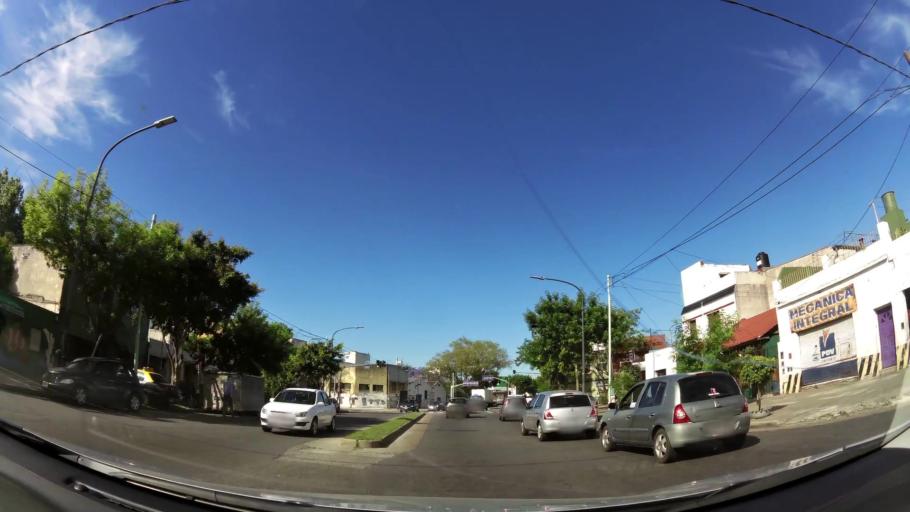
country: AR
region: Buenos Aires
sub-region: Partido de General San Martin
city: General San Martin
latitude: -34.5519
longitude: -58.4889
